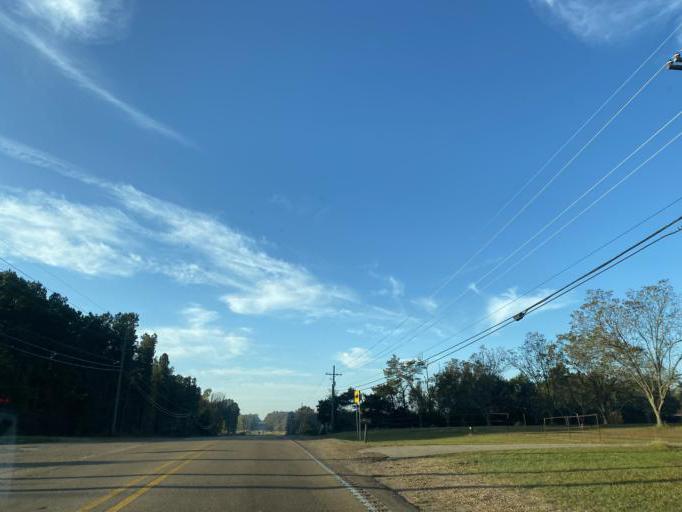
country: US
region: Mississippi
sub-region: Madison County
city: Madison
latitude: 32.4927
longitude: -90.0954
